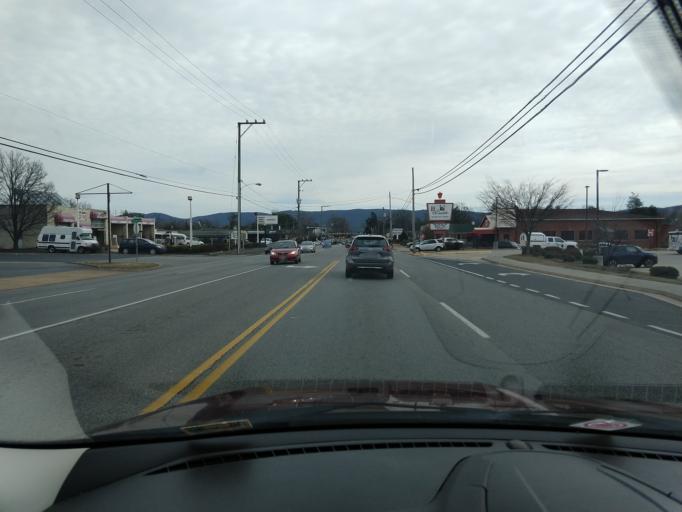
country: US
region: Virginia
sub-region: City of Waynesboro
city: Waynesboro
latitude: 38.0771
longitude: -78.9158
